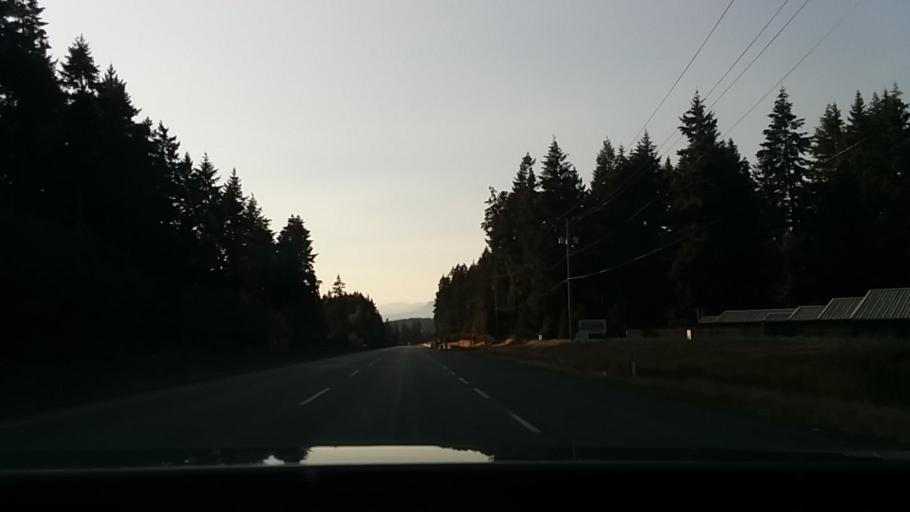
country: CA
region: British Columbia
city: Duncan
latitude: 48.7001
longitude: -123.5972
